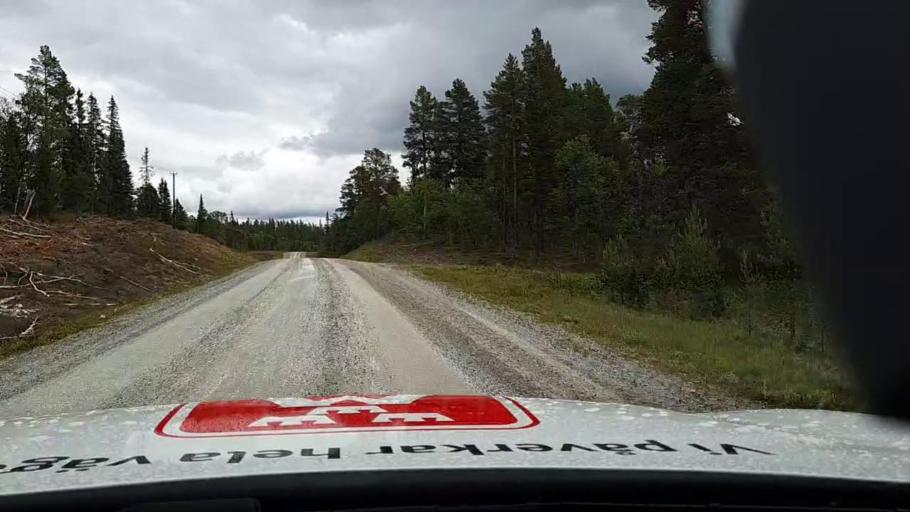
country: SE
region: Jaemtland
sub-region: Are Kommun
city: Are
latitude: 62.6652
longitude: 12.9339
